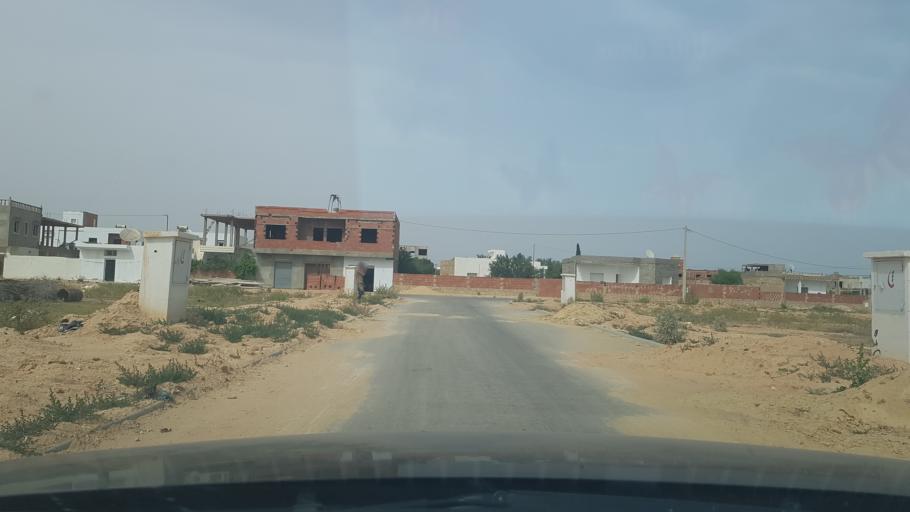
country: TN
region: Safaqis
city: Sfax
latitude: 34.8240
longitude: 10.7386
